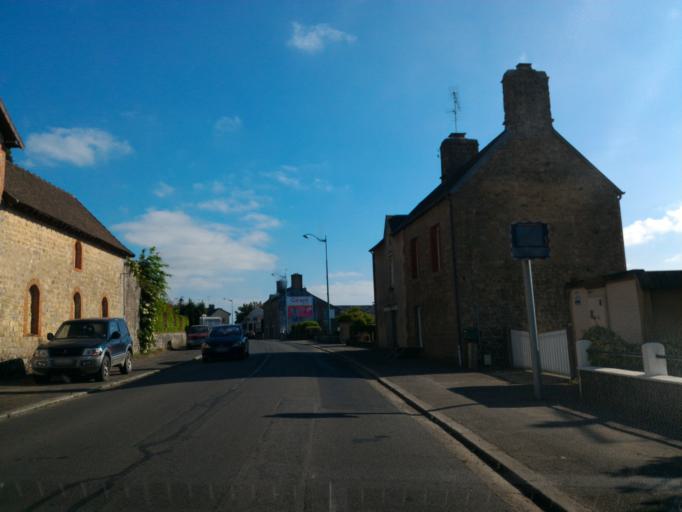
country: FR
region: Lower Normandy
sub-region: Departement de la Manche
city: La Haye-Pesnel
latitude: 48.7991
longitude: -1.3983
